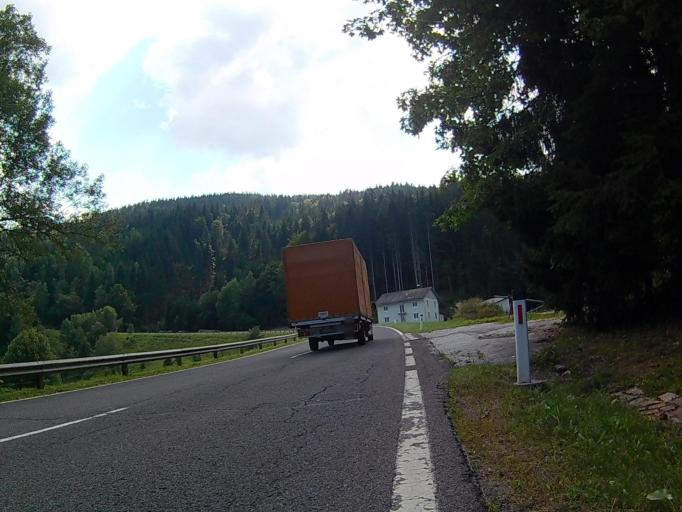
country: AT
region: Styria
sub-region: Politischer Bezirk Deutschlandsberg
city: Soboth
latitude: 46.7062
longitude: 15.0916
